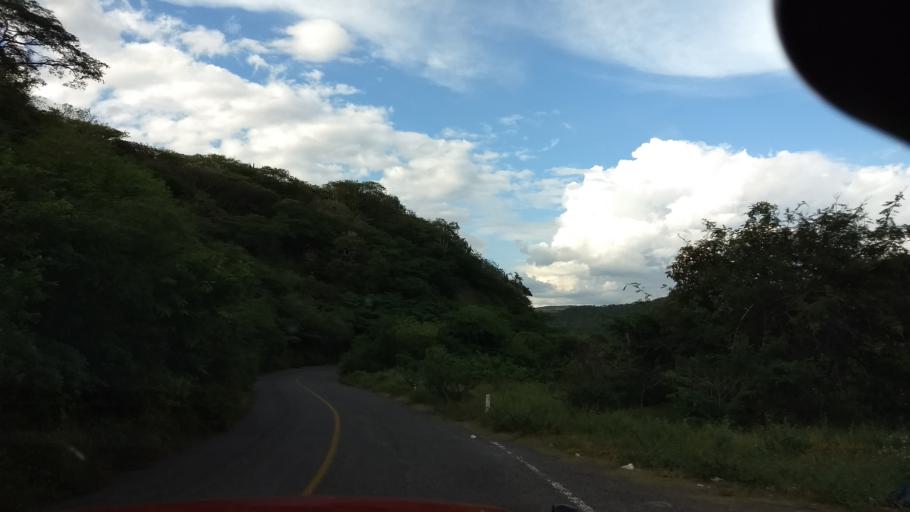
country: MX
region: Colima
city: Suchitlan
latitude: 19.4548
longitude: -103.8213
